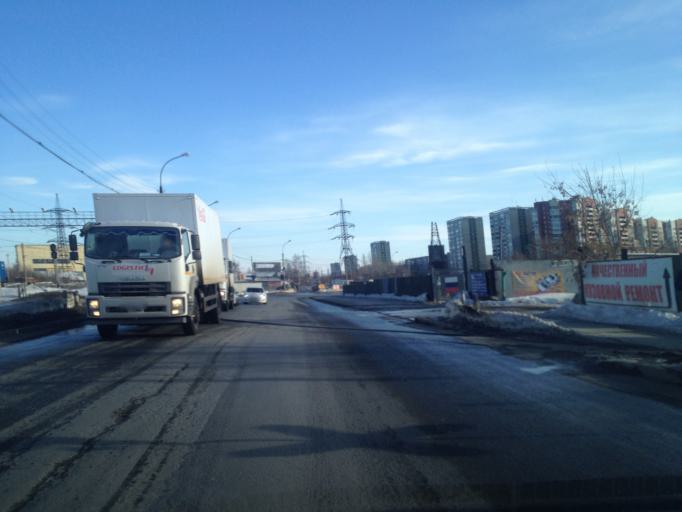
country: RU
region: Sverdlovsk
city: Yekaterinburg
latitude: 56.8785
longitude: 60.5517
